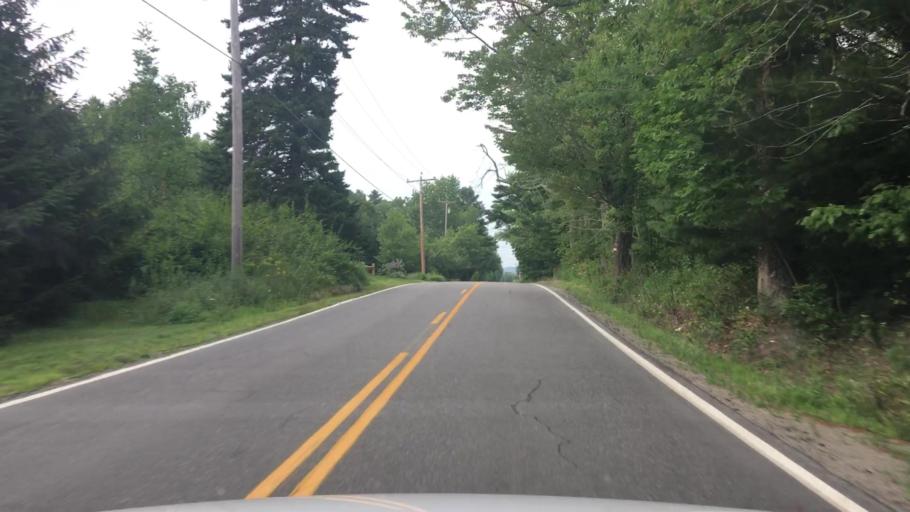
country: US
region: Maine
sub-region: Knox County
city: Washington
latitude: 44.2980
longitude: -69.3620
